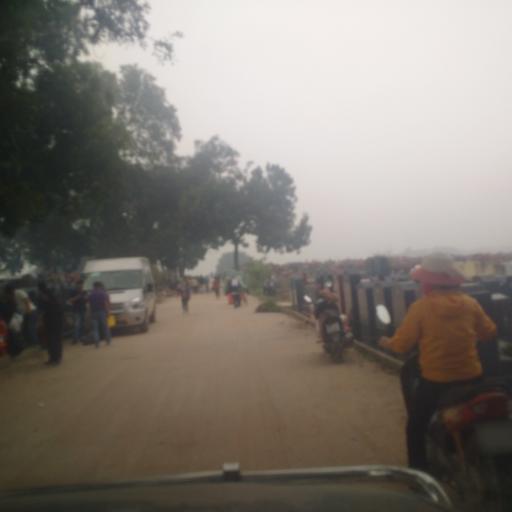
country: VN
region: Ha Noi
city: Tay Dang
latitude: 21.2144
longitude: 105.3644
